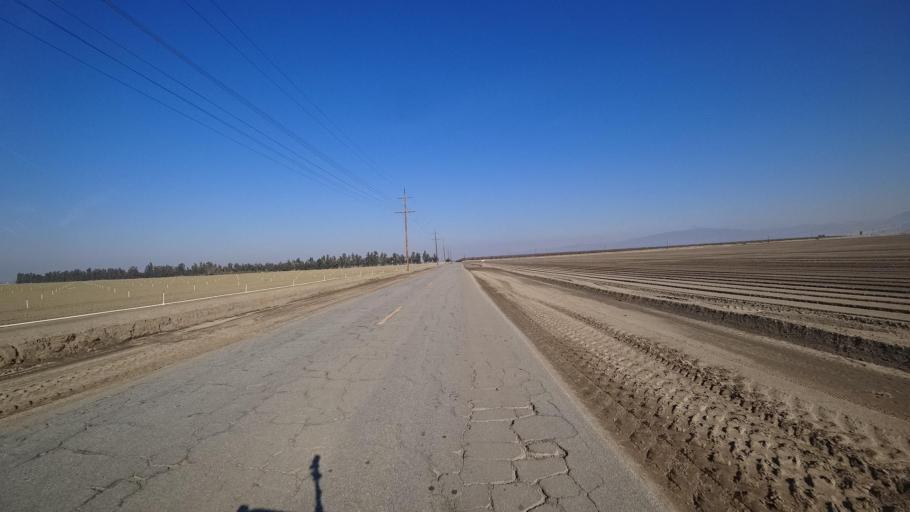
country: US
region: California
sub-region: Kern County
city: Arvin
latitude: 35.1318
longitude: -118.8777
